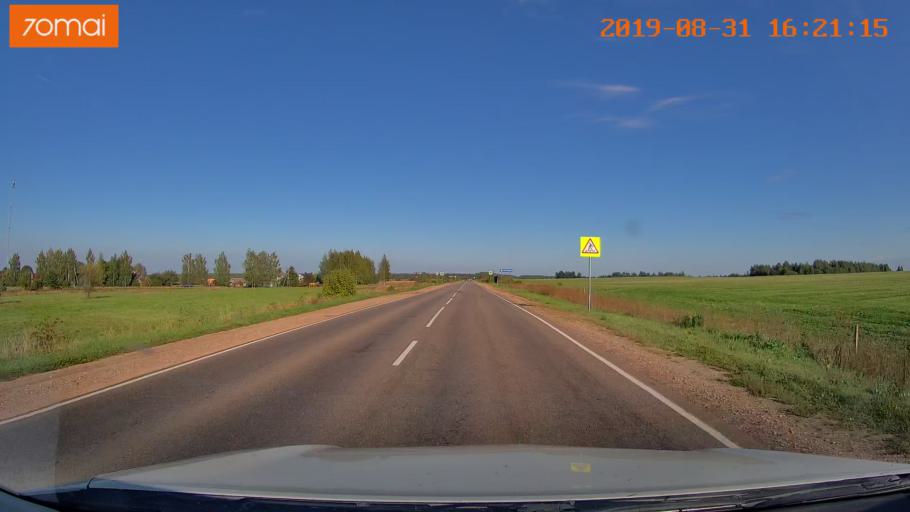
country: RU
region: Kaluga
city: Babynino
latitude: 54.5224
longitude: 35.6266
